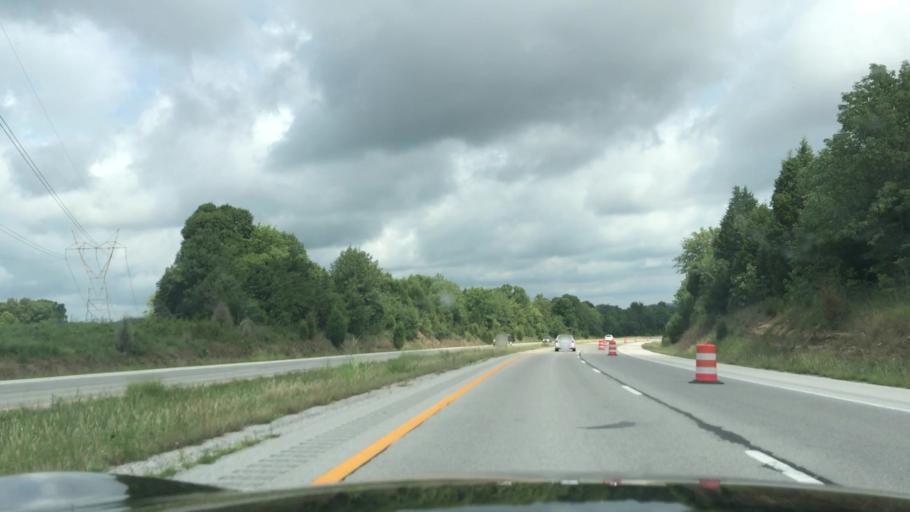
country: US
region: Kentucky
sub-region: Butler County
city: Morgantown
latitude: 37.1012
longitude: -86.6384
